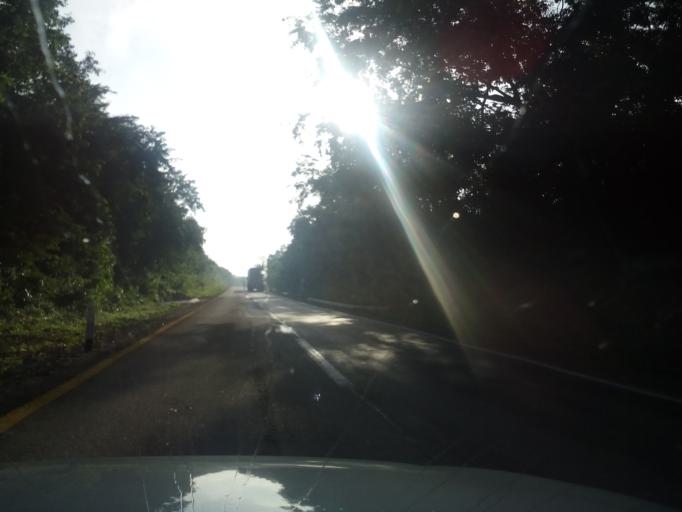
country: MX
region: Yucatan
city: Tunkas
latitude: 20.7658
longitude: -88.8043
